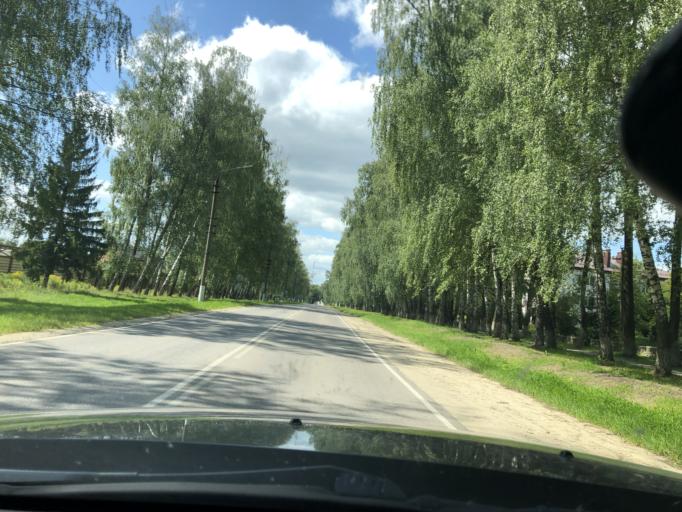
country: RU
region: Tula
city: Gorelki
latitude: 54.3367
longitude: 37.5614
